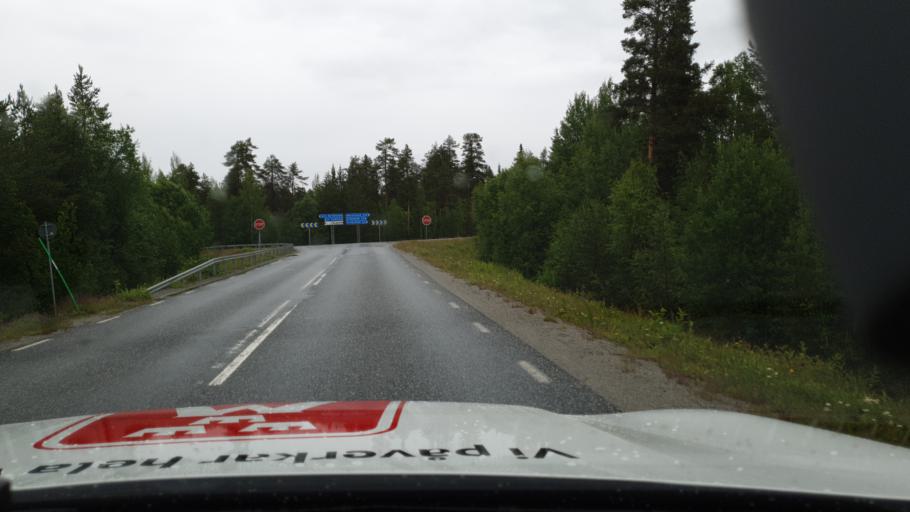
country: SE
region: Vaesterbotten
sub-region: Vilhelmina Kommun
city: Vilhelmina
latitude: 64.4350
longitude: 16.8042
